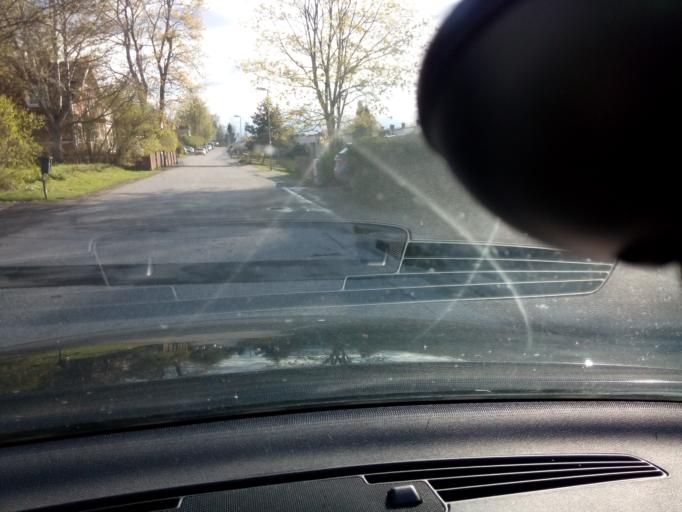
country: SE
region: Soedermanland
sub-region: Nykopings Kommun
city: Nykoping
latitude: 58.7810
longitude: 17.0981
